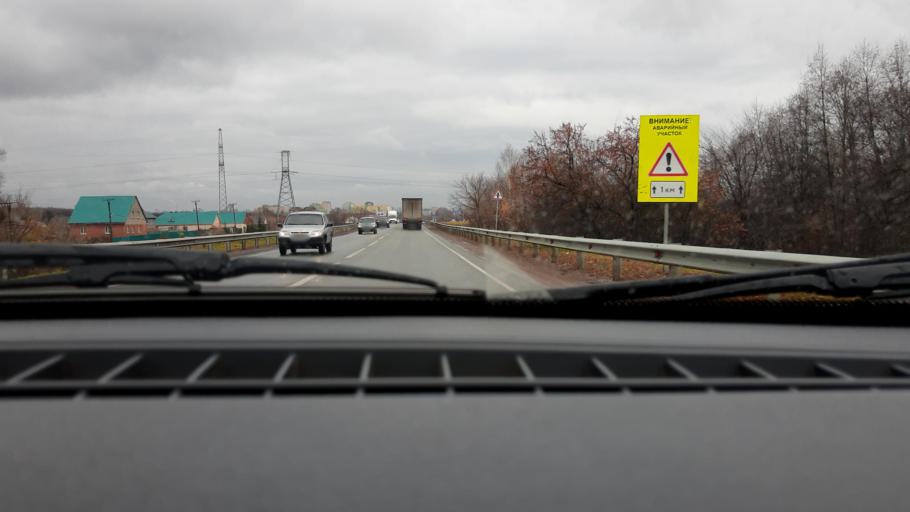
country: RU
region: Bashkortostan
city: Mikhaylovka
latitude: 54.8127
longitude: 55.8461
